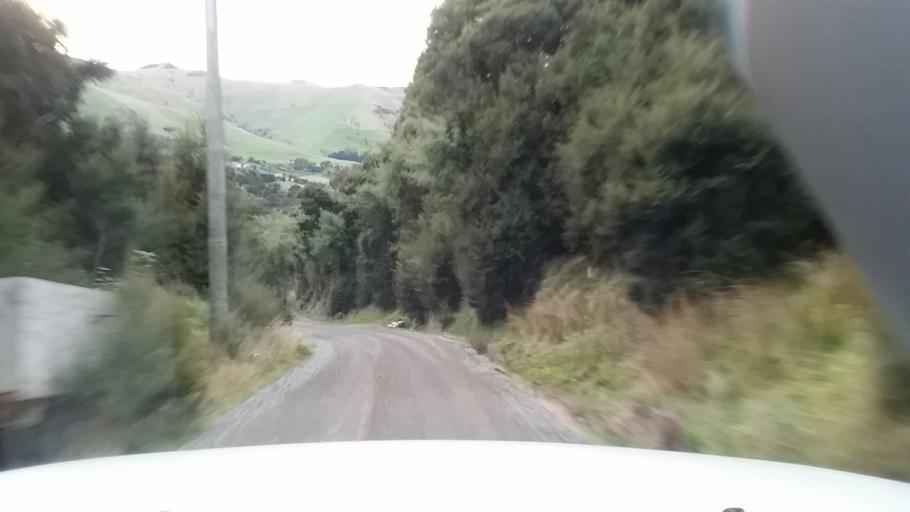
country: NZ
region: Canterbury
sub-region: Christchurch City
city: Christchurch
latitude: -43.7352
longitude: 172.7806
